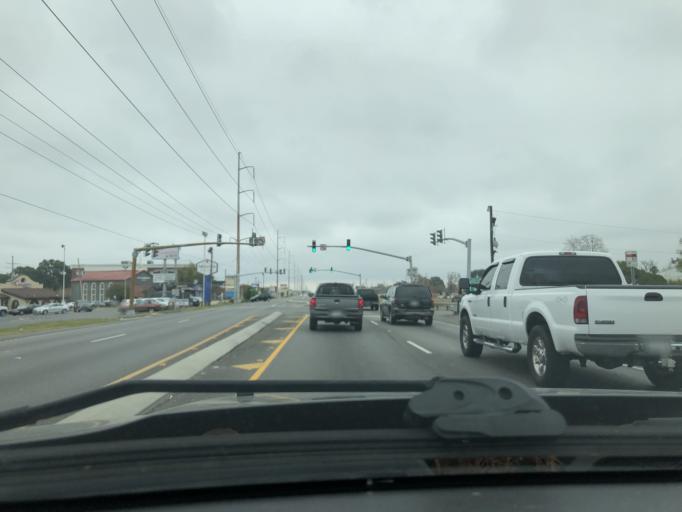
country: US
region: Louisiana
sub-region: Jefferson Parish
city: River Ridge
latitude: 29.9785
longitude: -90.2219
